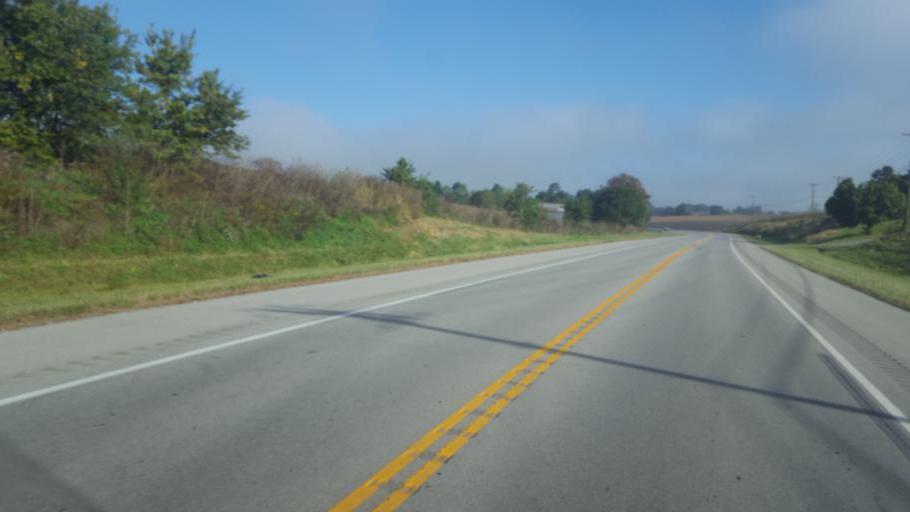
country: US
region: Kentucky
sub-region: Fleming County
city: Flemingsburg
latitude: 38.5231
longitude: -83.7547
